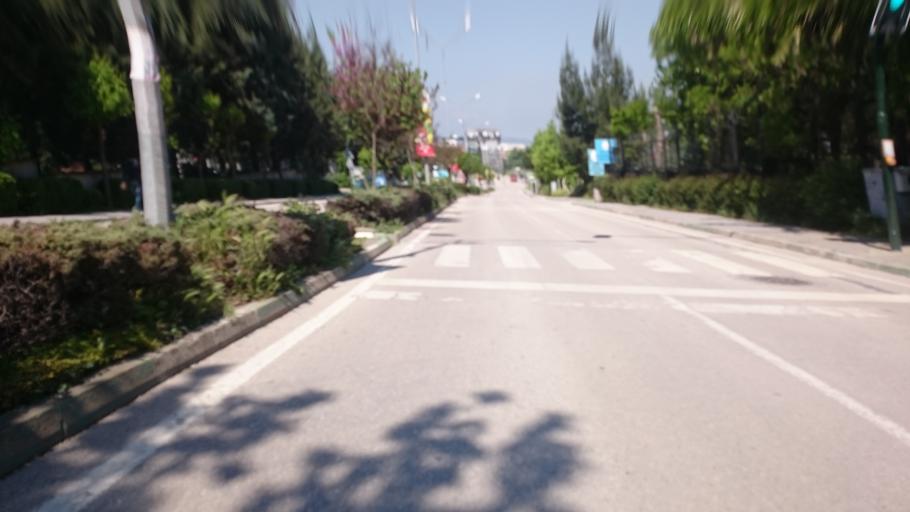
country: TR
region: Bursa
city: Yildirim
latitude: 40.2256
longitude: 28.9747
